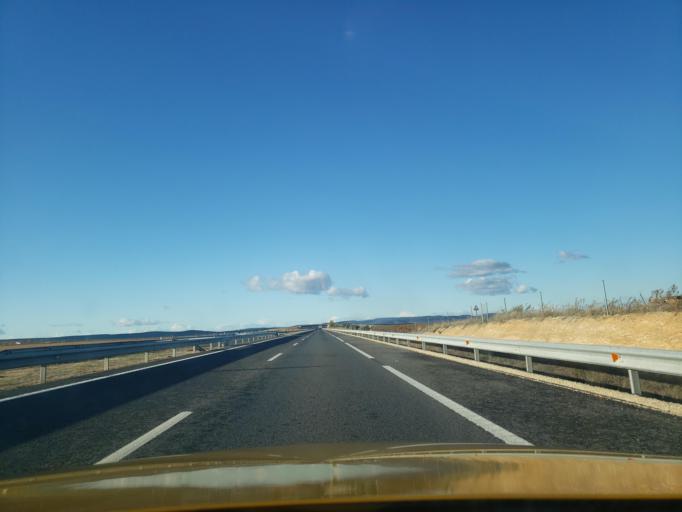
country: ES
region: Castille-La Mancha
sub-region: Province of Toledo
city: Turleque
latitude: 39.5378
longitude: -3.6650
